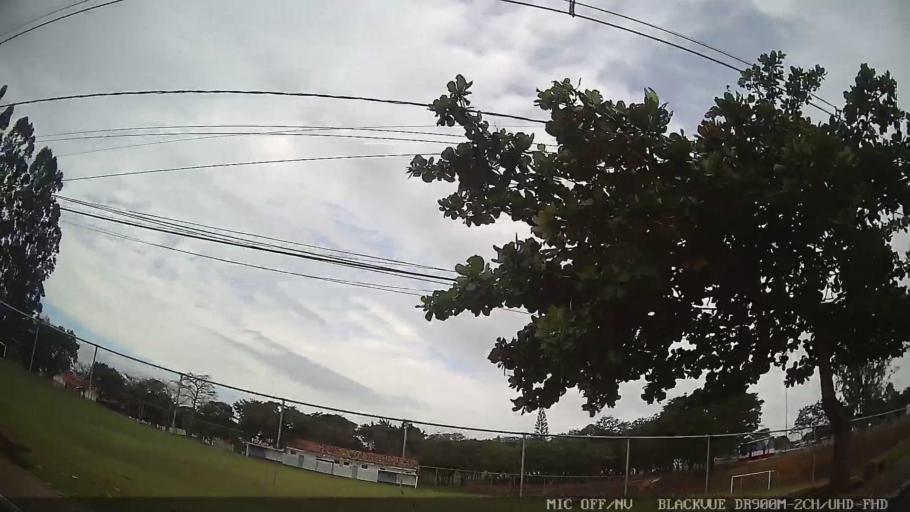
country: BR
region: Sao Paulo
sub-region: Salto
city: Salto
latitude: -23.2230
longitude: -47.2658
